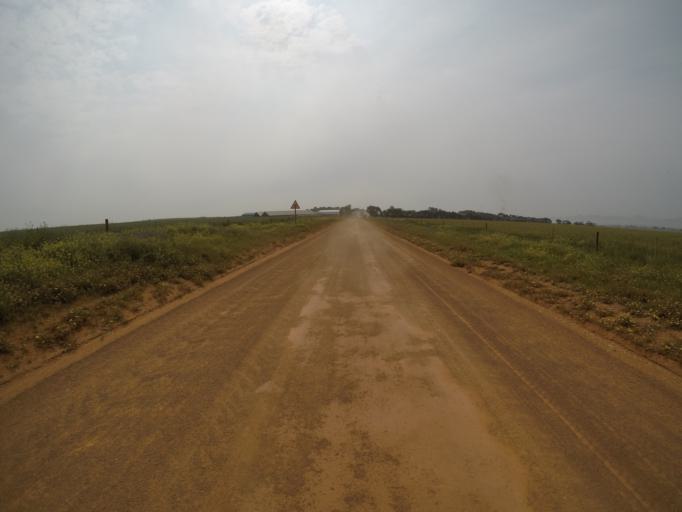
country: ZA
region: Western Cape
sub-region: City of Cape Town
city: Kraaifontein
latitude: -33.7088
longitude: 18.6891
